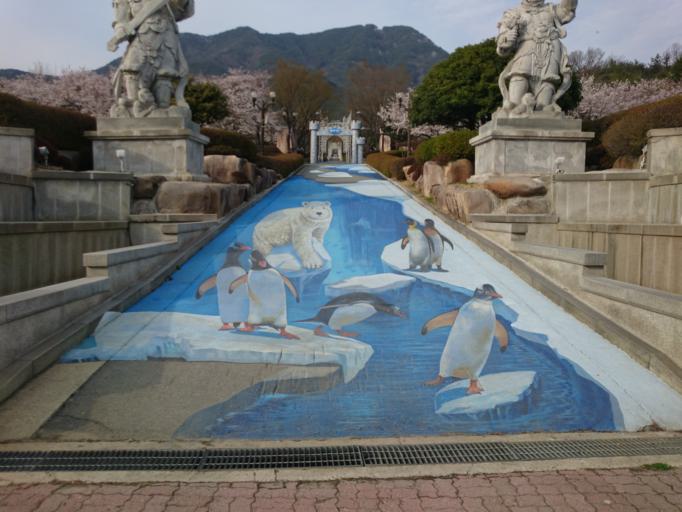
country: KR
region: Gyeongsangnam-do
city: Changnyeong
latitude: 35.4403
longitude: 128.5935
